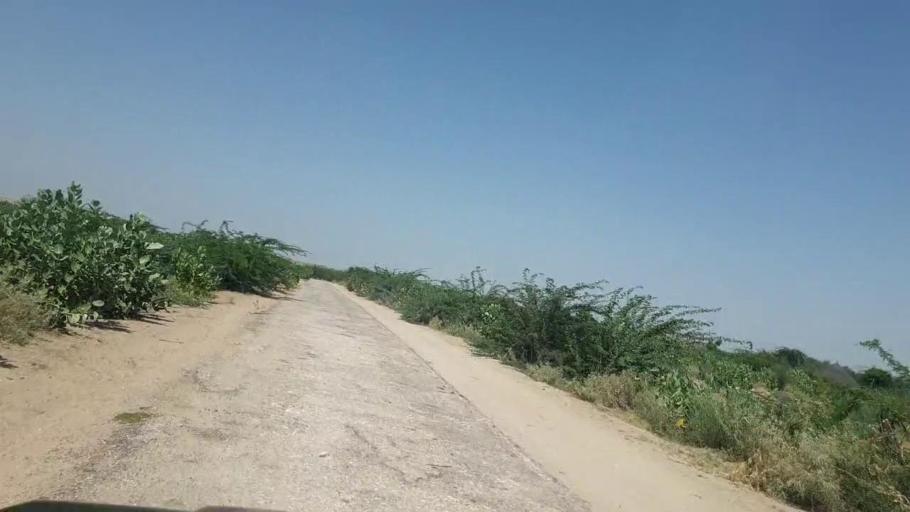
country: PK
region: Sindh
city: Chor
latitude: 25.4016
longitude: 70.3105
